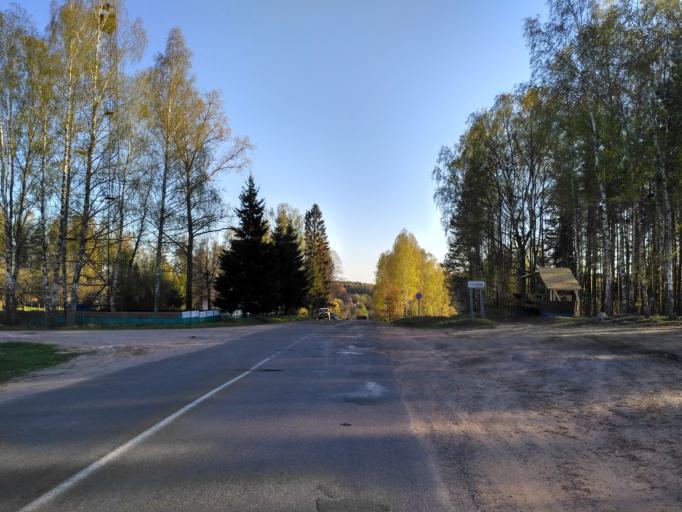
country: BY
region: Minsk
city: Loshnitsa
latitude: 54.4605
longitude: 28.6431
